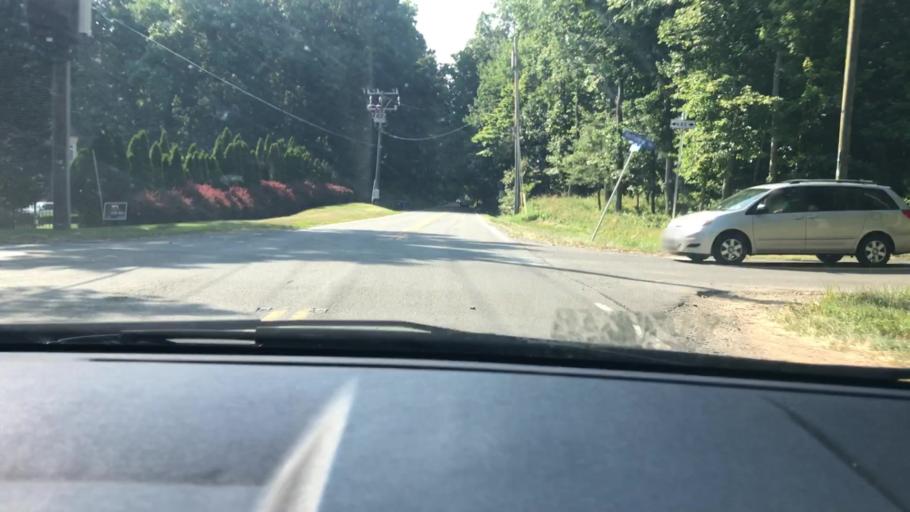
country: US
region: Virginia
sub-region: Fairfax County
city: Tysons Corner
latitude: 38.9610
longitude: -77.2401
